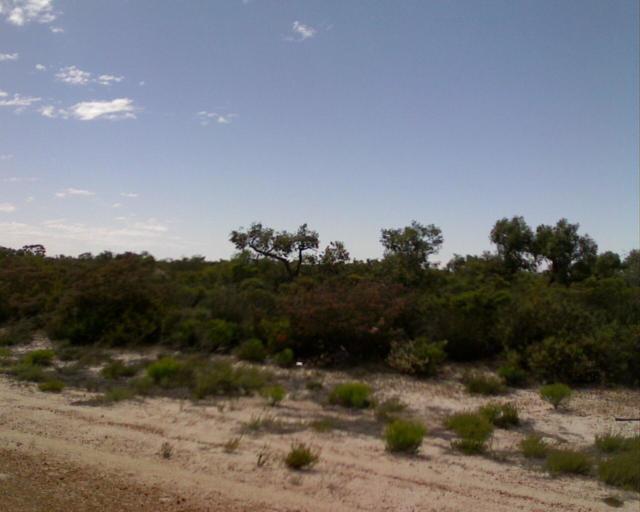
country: AU
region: Western Australia
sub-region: Dandaragan
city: Jurien Bay
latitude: -30.0742
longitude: 115.6246
